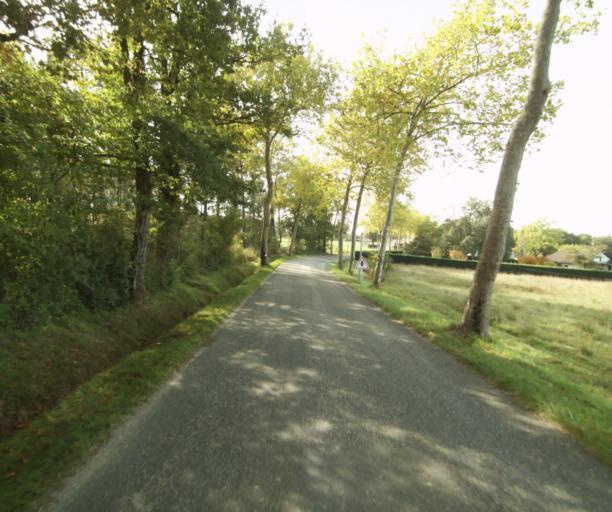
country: FR
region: Midi-Pyrenees
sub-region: Departement du Gers
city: Eauze
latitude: 43.9279
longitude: 0.0913
